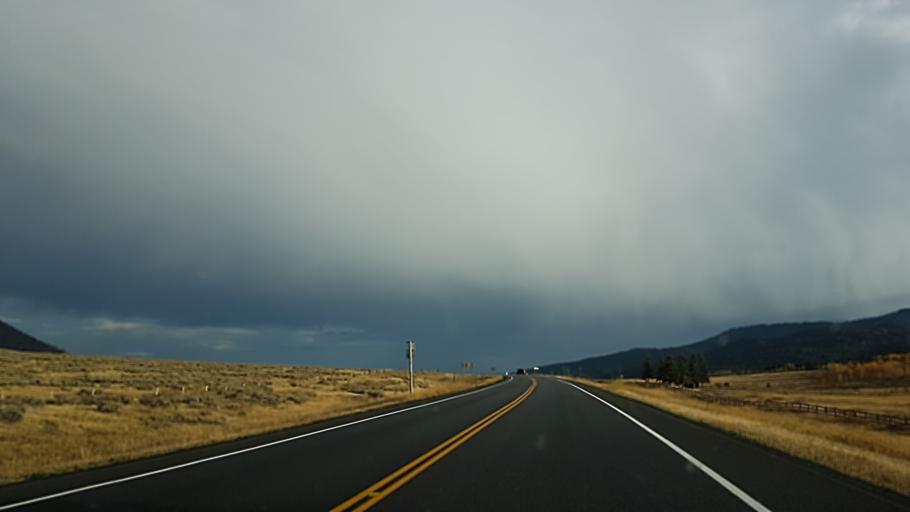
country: US
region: Montana
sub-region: Gallatin County
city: West Yellowstone
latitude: 44.7129
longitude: -111.4703
